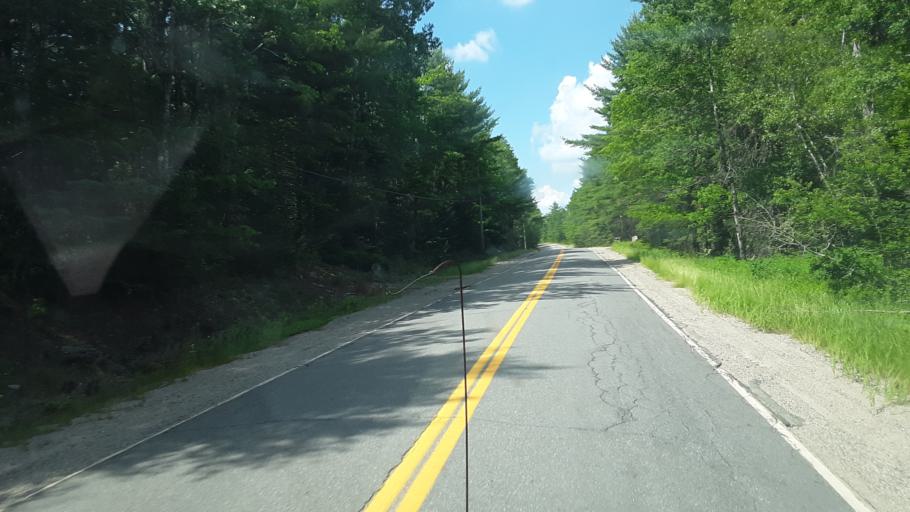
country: US
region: Maine
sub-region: Washington County
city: Machias
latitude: 44.8823
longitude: -67.6221
